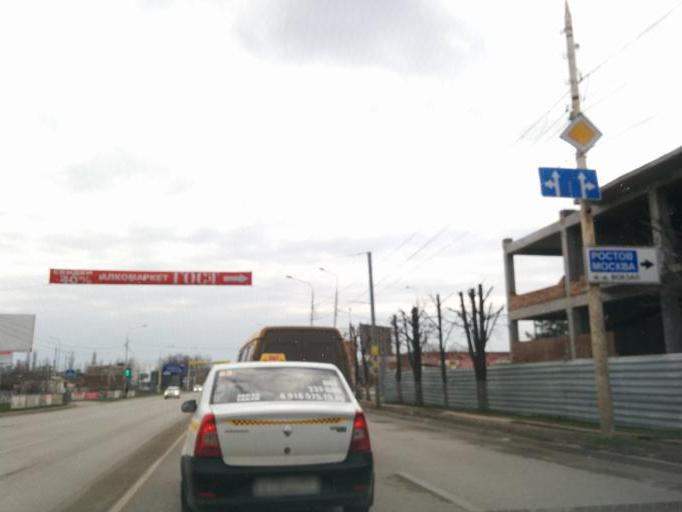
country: RU
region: Rostov
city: Shakhty
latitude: 47.6989
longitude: 40.2087
